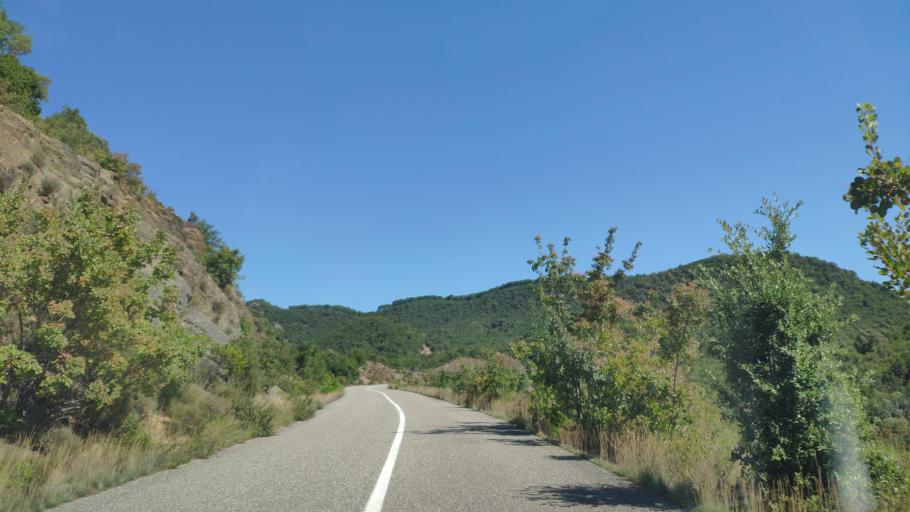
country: GR
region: Central Greece
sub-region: Nomos Evrytanias
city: Kerasochori
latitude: 38.9821
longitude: 21.4933
